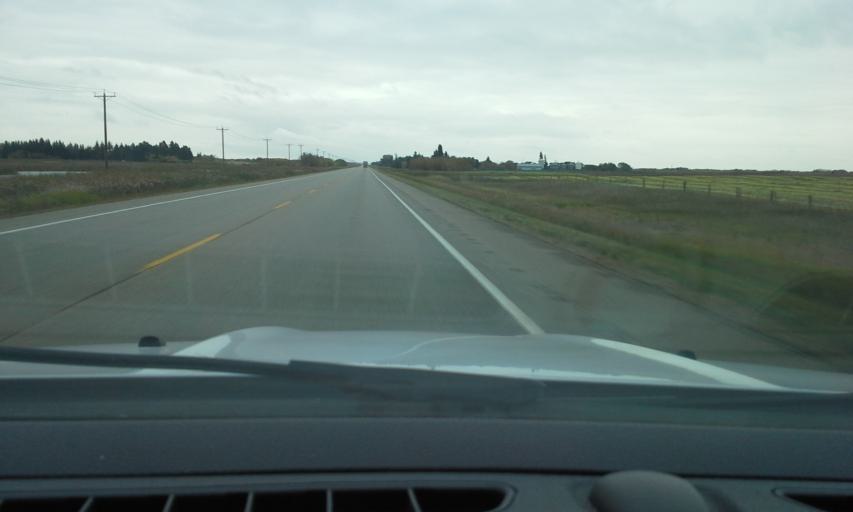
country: CA
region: Saskatchewan
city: Lloydminster
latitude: 53.2780
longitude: -109.8642
